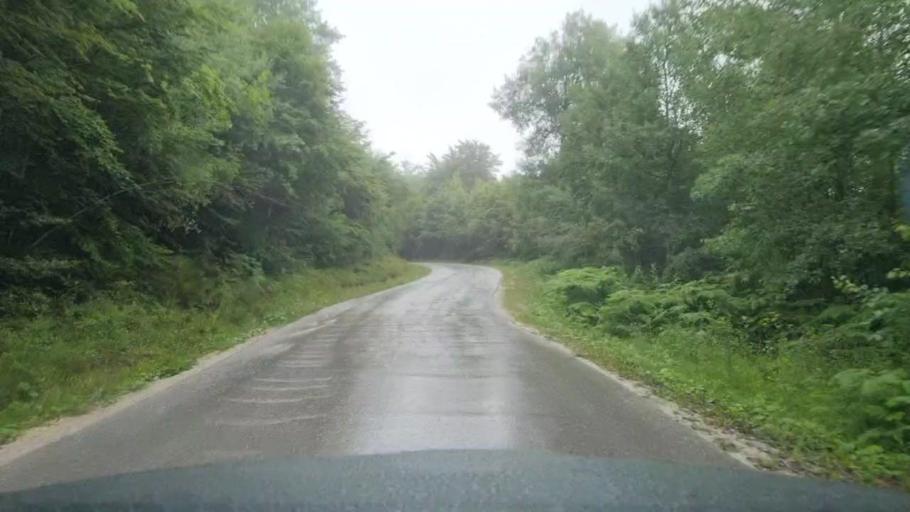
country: BA
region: Republika Srpska
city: Koran
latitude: 43.6465
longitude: 18.6066
